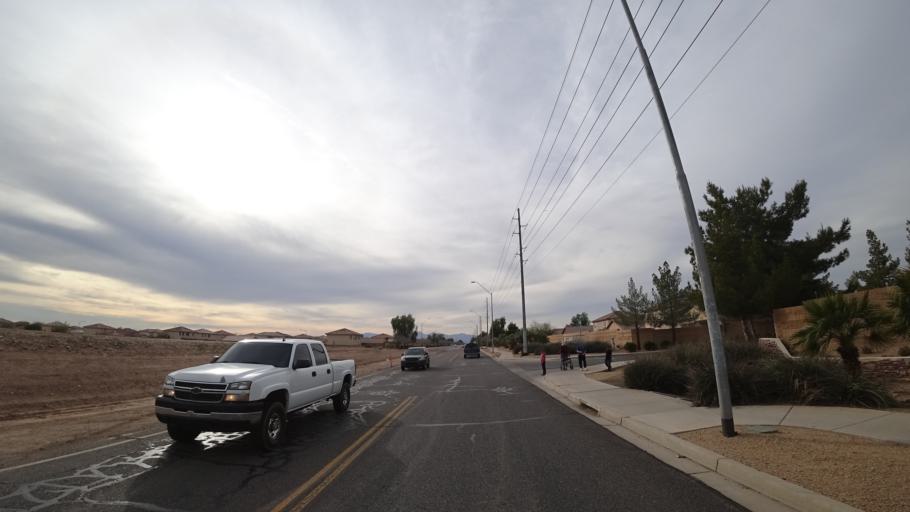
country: US
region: Arizona
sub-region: Maricopa County
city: El Mirage
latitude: 33.5946
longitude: -112.3287
